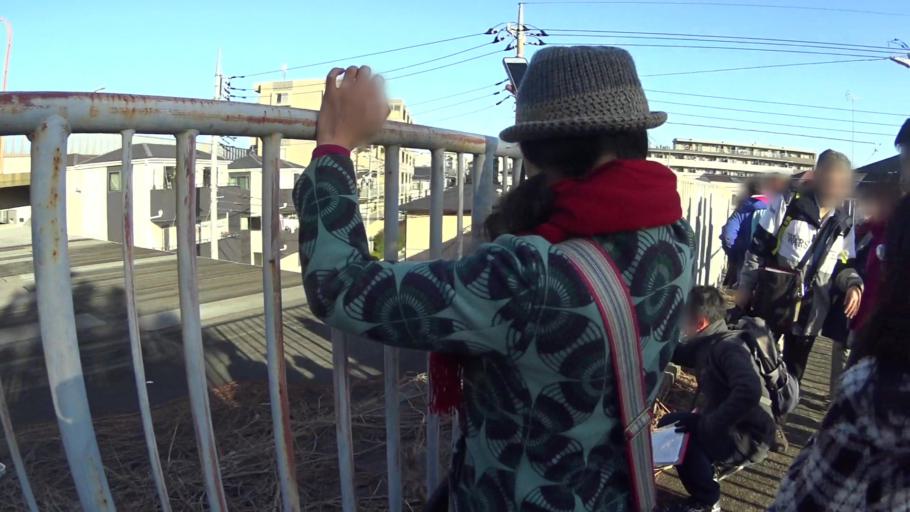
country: JP
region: Saitama
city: Yono
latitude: 35.8640
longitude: 139.6420
